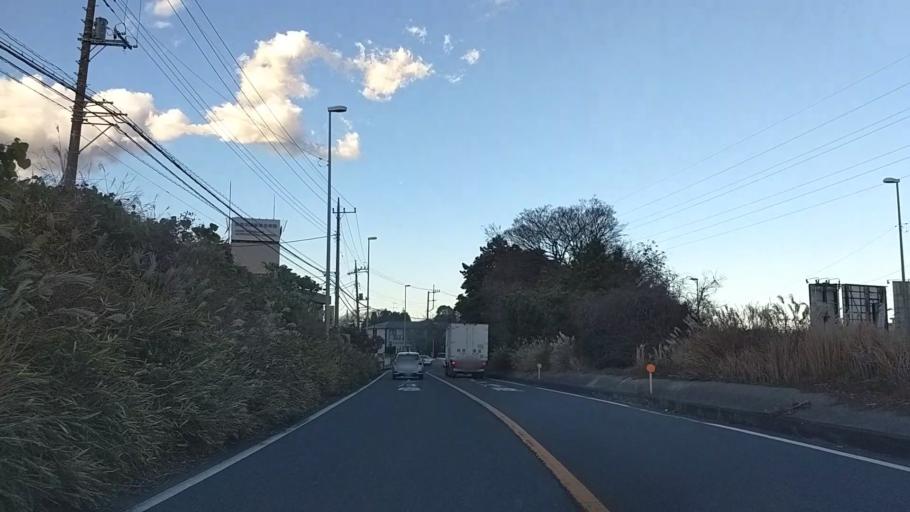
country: JP
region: Kanagawa
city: Fujisawa
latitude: 35.3834
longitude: 139.5146
